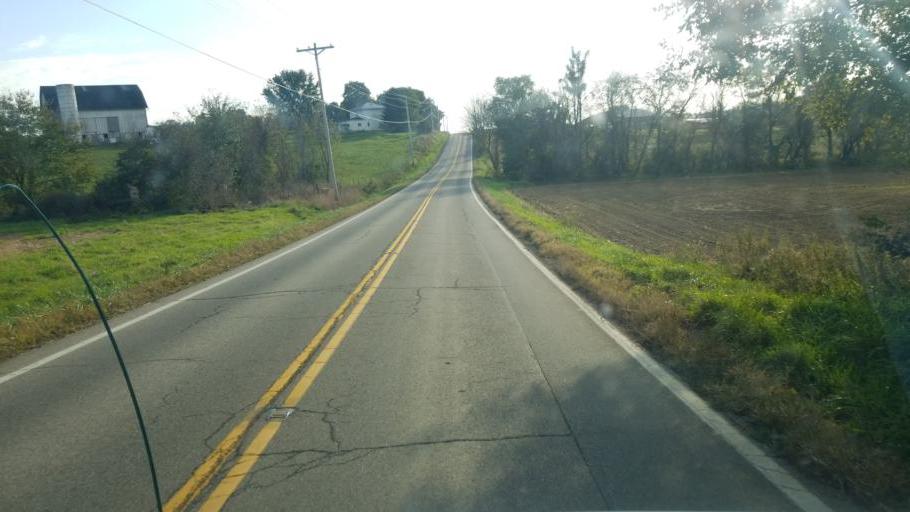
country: US
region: Ohio
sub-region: Wayne County
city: Shreve
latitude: 40.6169
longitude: -82.0953
